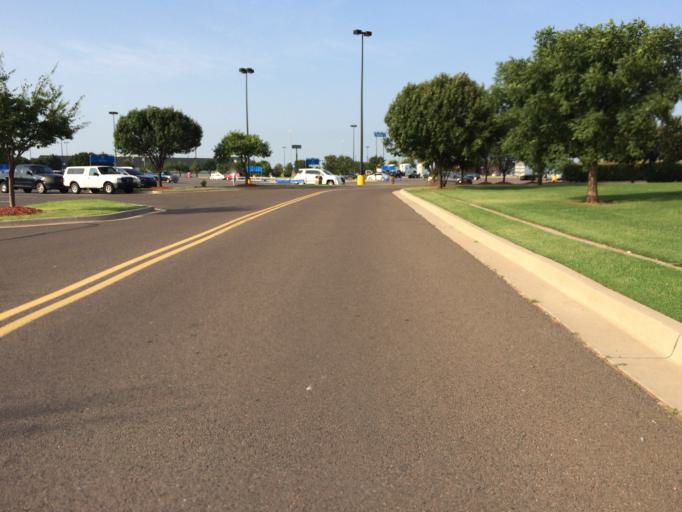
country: US
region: Oklahoma
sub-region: Cleveland County
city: Norman
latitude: 35.2225
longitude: -97.4823
